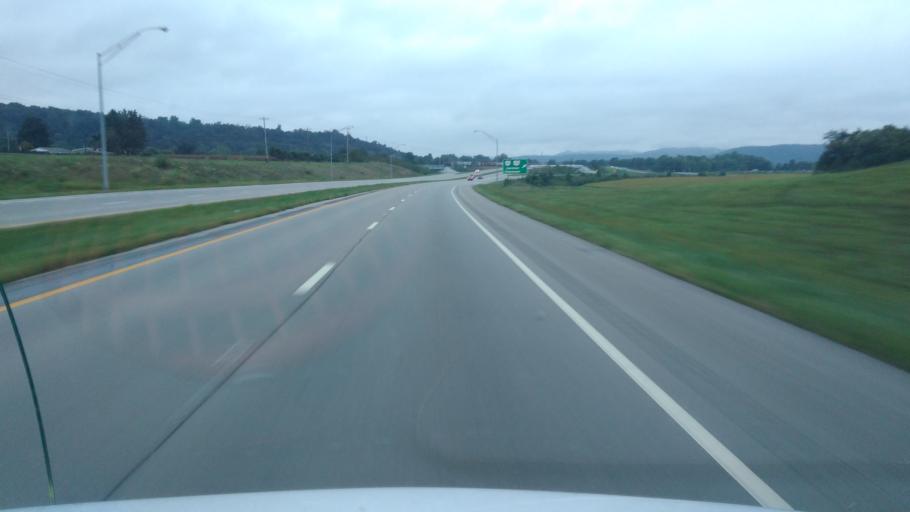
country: US
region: Ohio
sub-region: Pike County
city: Piketon
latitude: 39.0537
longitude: -83.0204
